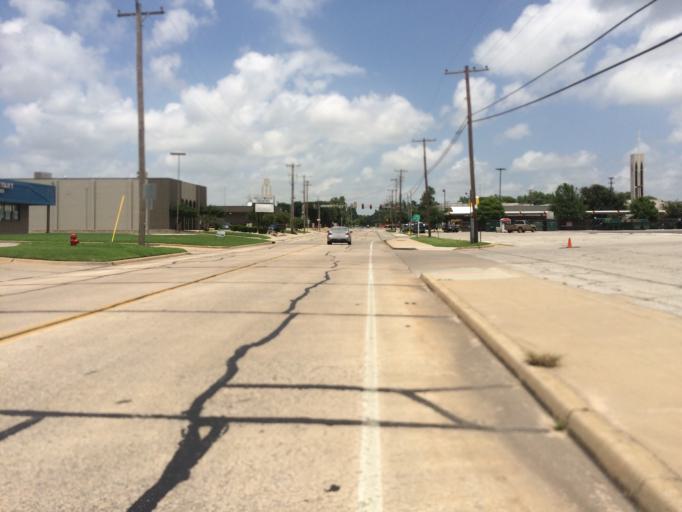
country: US
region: Oklahoma
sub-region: Cleveland County
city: Norman
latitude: 35.2024
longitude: -97.4678
